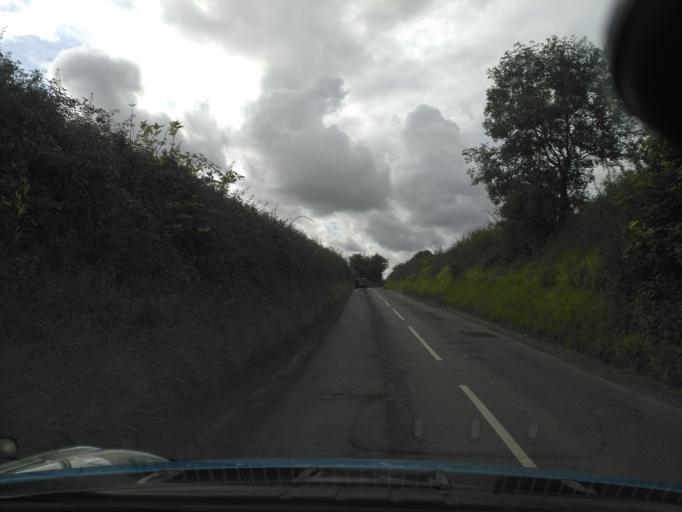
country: GB
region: England
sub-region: Oxfordshire
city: Stanford in the Vale
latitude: 51.5824
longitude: -1.5354
